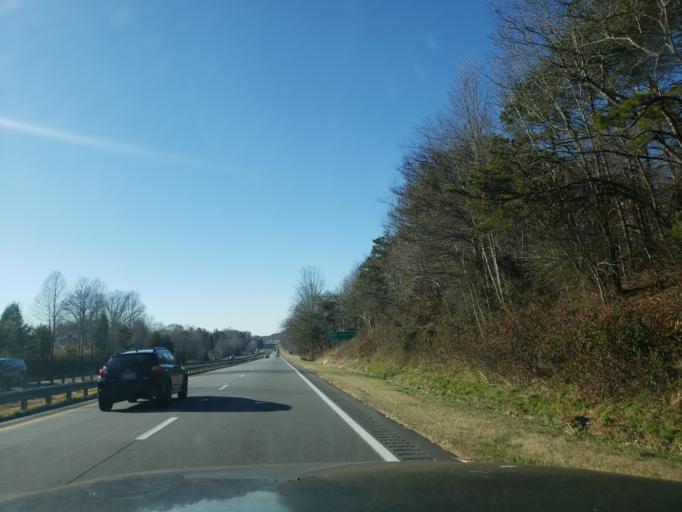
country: US
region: North Carolina
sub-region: Yadkin County
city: Yadkinville
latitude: 36.1172
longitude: -80.6168
